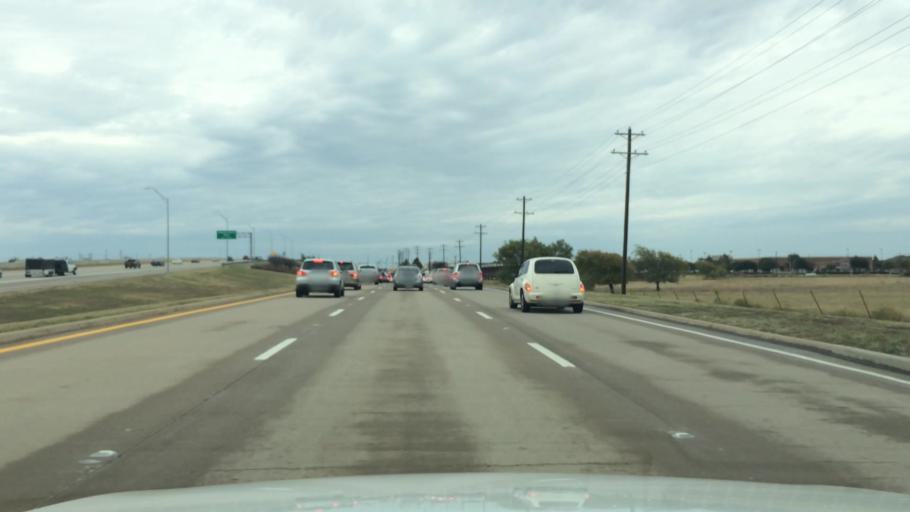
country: US
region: Texas
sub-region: Collin County
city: Frisco
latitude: 33.1098
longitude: -96.7728
